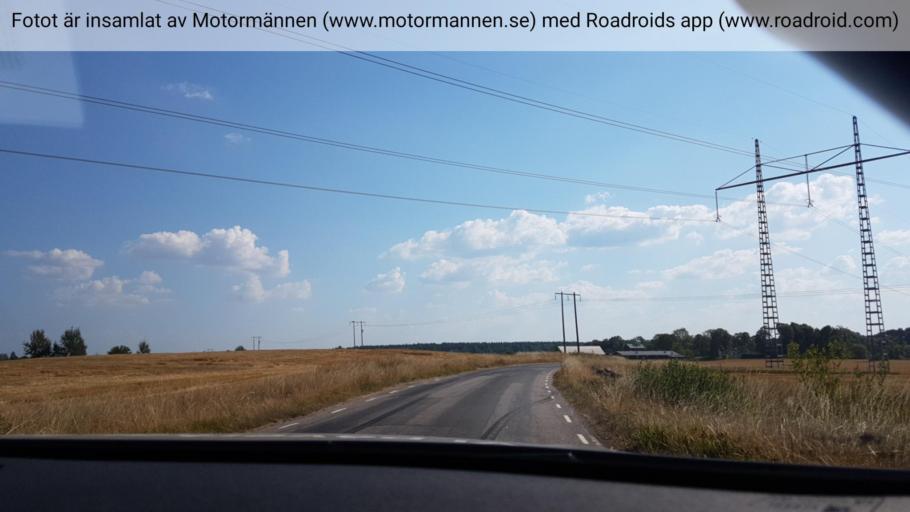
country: SE
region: Vaestra Goetaland
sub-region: Skovde Kommun
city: Stopen
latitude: 58.5896
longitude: 13.8626
